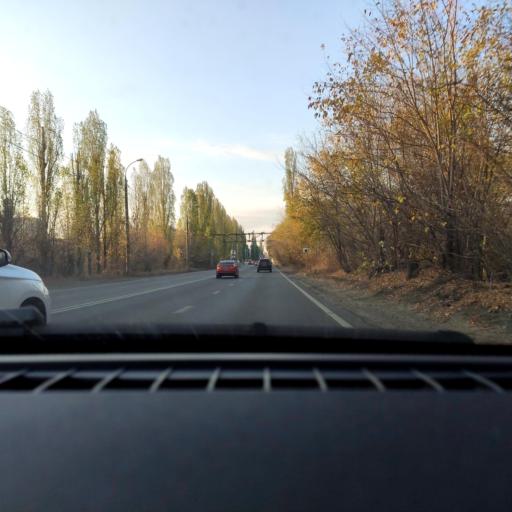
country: RU
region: Voronezj
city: Maslovka
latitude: 51.6041
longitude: 39.2542
